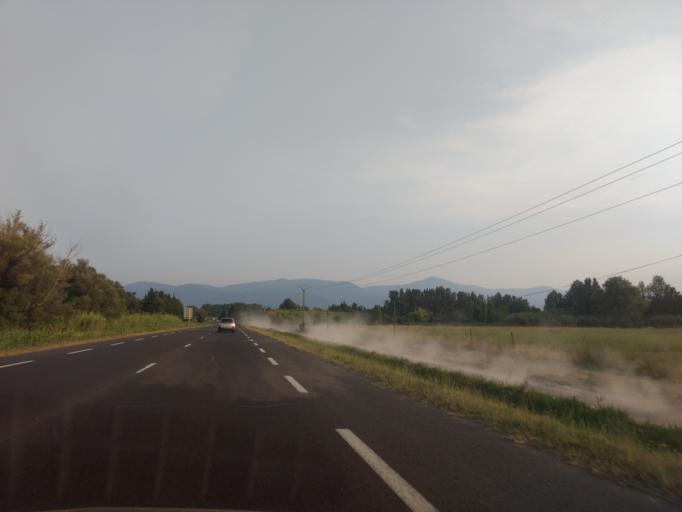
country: FR
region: Languedoc-Roussillon
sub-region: Departement des Pyrenees-Orientales
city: Latour-Bas-Elne
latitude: 42.6052
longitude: 3.0244
